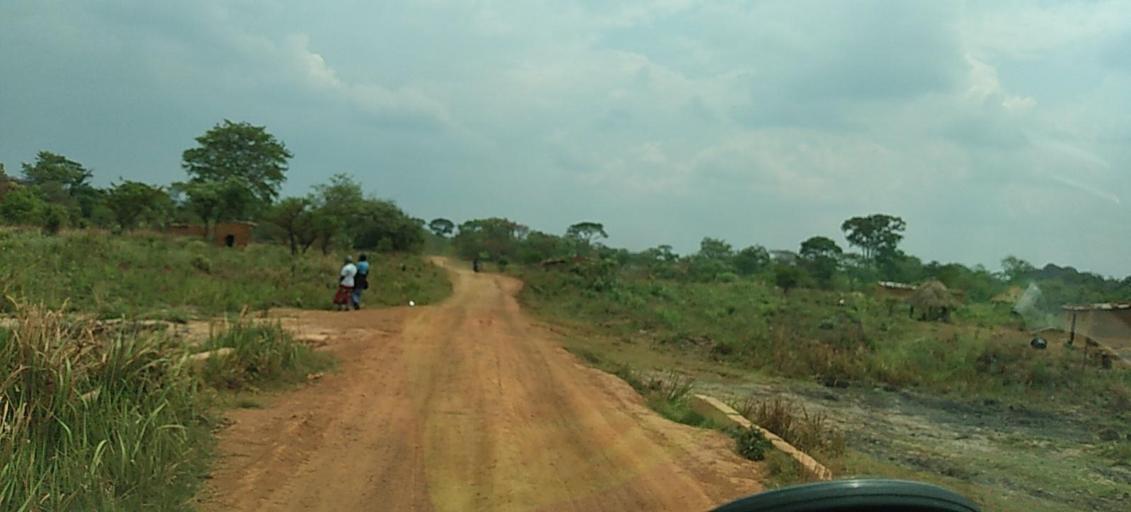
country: ZM
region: North-Western
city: Kansanshi
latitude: -11.9929
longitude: 26.2813
